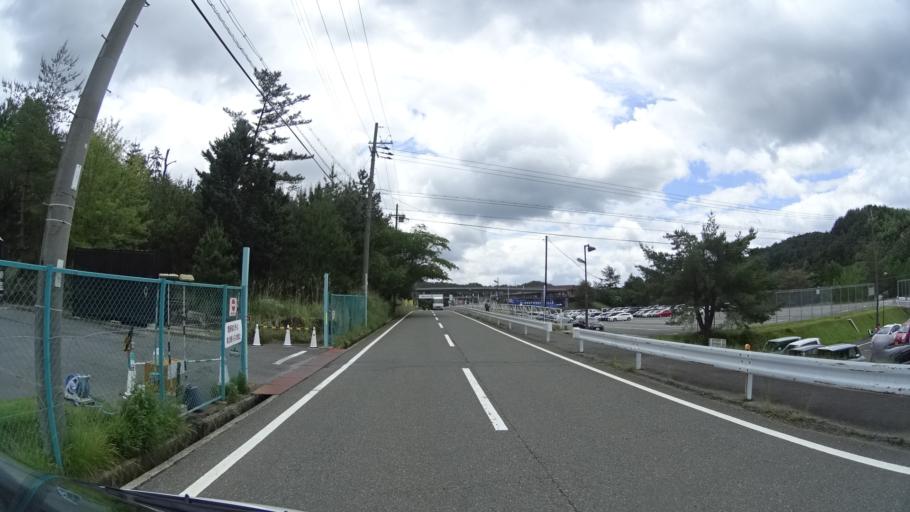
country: JP
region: Hyogo
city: Sasayama
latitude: 35.0335
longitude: 135.3964
